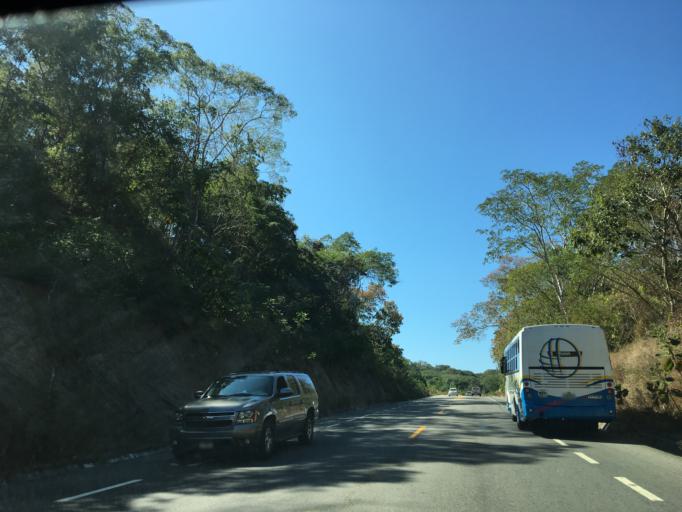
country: MX
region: Oaxaca
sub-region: Santa Maria Huatulco
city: Sector H Tres
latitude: 15.7786
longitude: -96.1808
